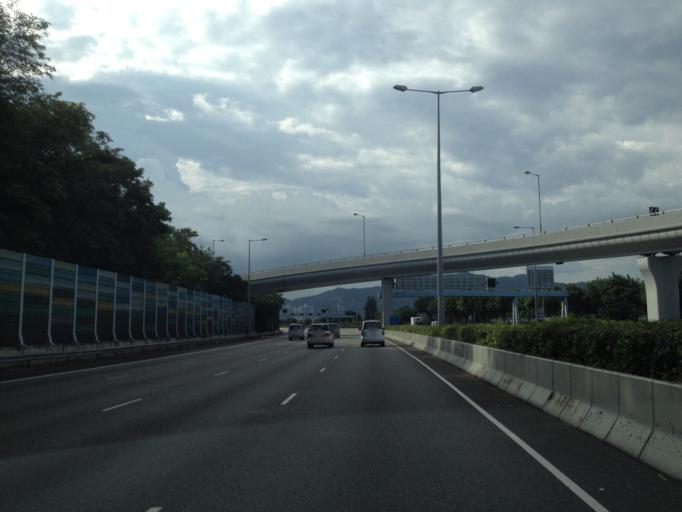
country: HK
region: Tai Po
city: Tai Po
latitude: 22.4361
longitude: 114.1989
